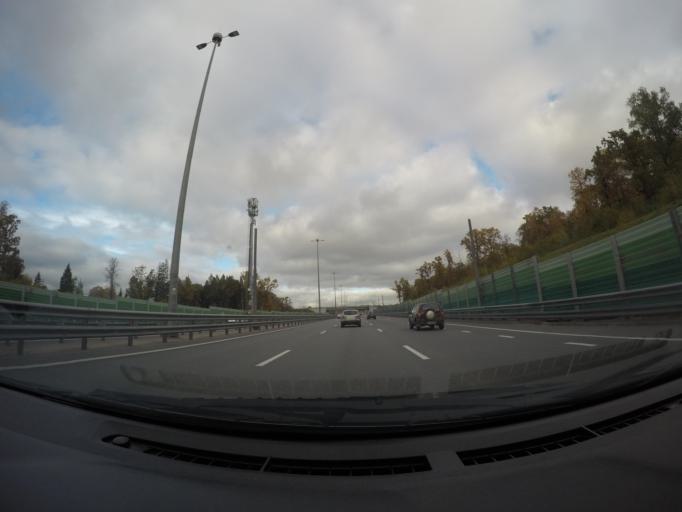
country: RU
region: Moskovskaya
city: Odintsovo
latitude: 55.6865
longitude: 37.2446
